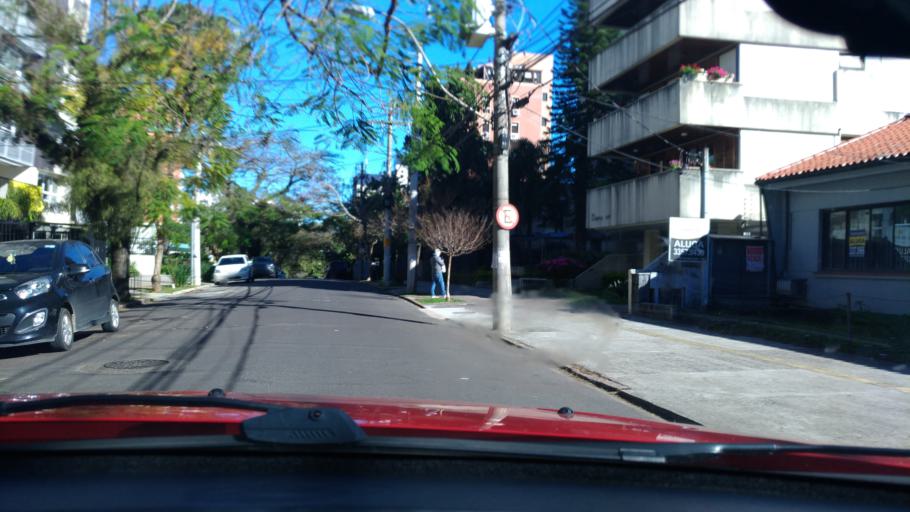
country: BR
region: Rio Grande do Sul
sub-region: Porto Alegre
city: Porto Alegre
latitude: -30.0178
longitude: -51.1876
